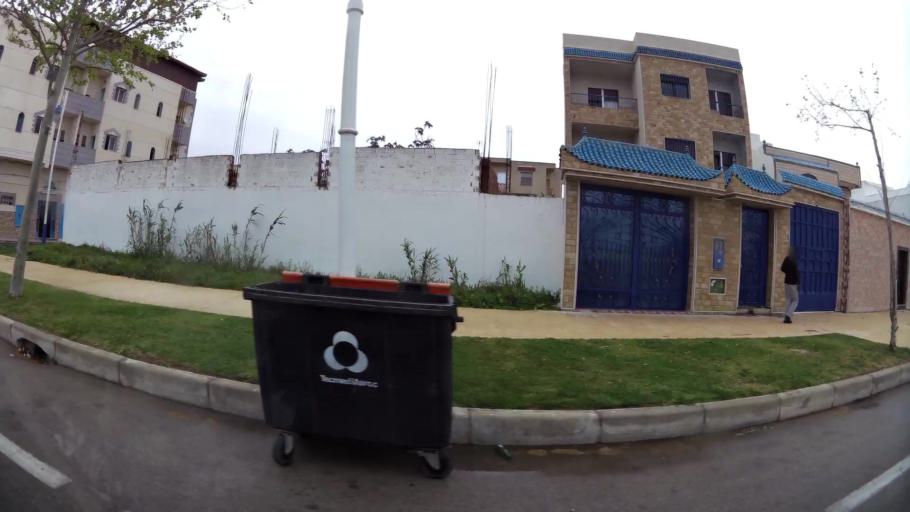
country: MA
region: Tanger-Tetouan
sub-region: Tetouan
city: Martil
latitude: 35.6383
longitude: -5.2902
